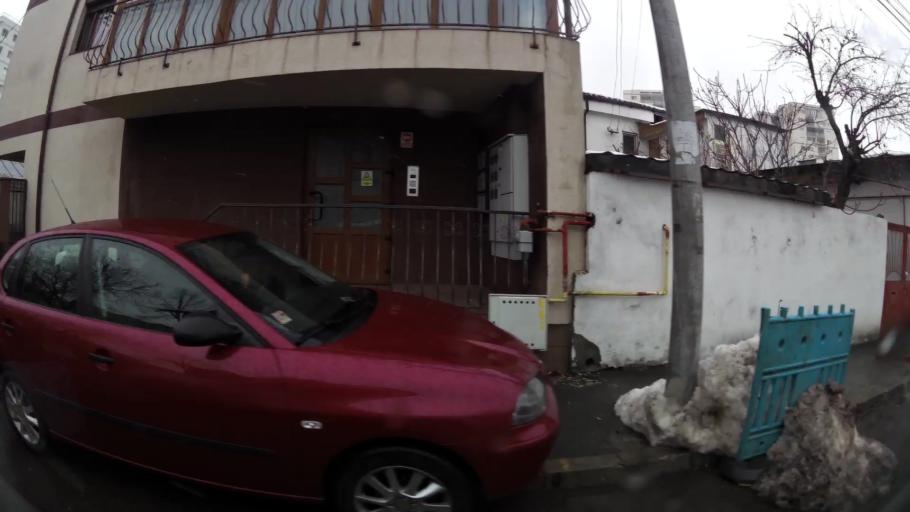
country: RO
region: Ilfov
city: Dobroesti
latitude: 44.4187
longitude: 26.1823
